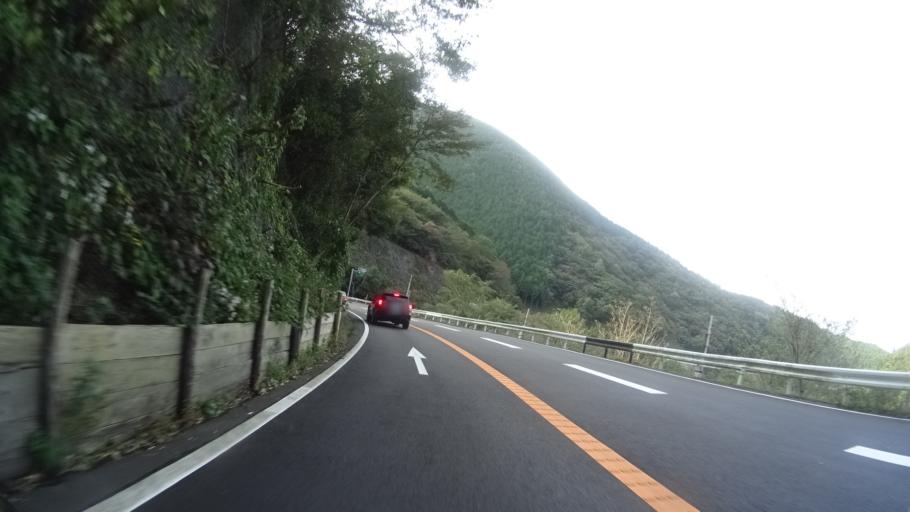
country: JP
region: Oita
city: Beppu
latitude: 33.2797
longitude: 131.4523
